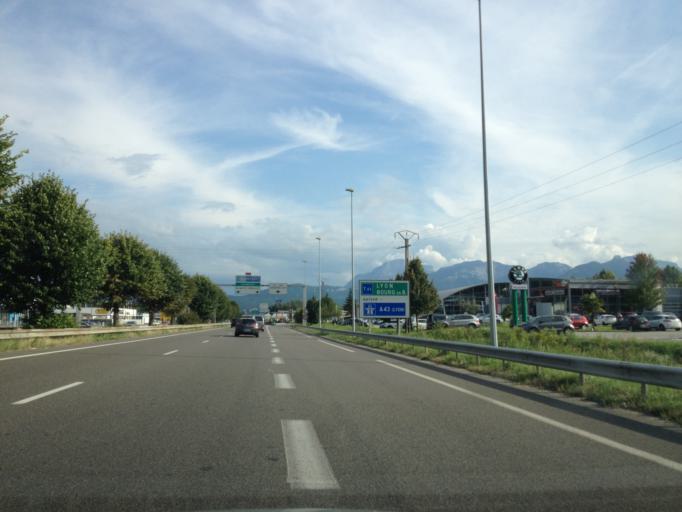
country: FR
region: Rhone-Alpes
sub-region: Departement de la Savoie
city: La Motte-Servolex
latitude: 45.6127
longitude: 5.8853
